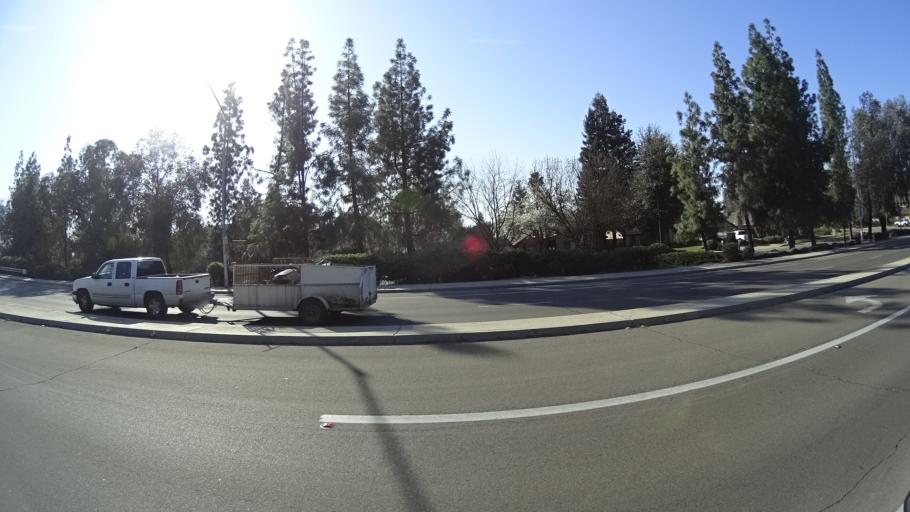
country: US
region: California
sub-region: Fresno County
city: Clovis
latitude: 36.8610
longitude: -119.7935
